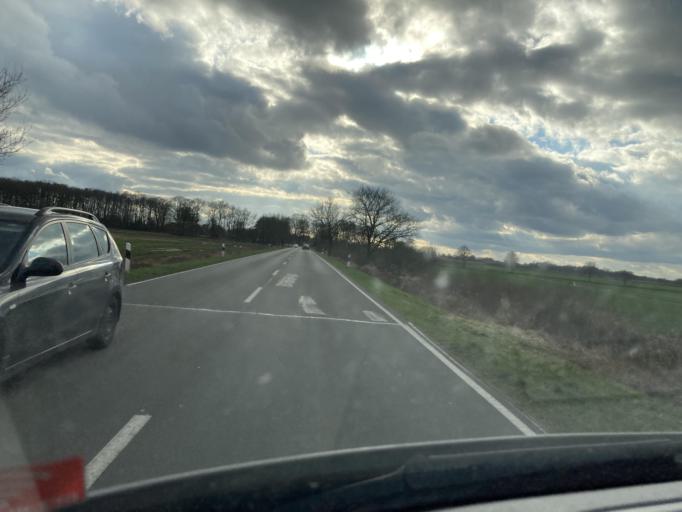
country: DE
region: Lower Saxony
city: Filsum
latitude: 53.1945
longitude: 7.6217
